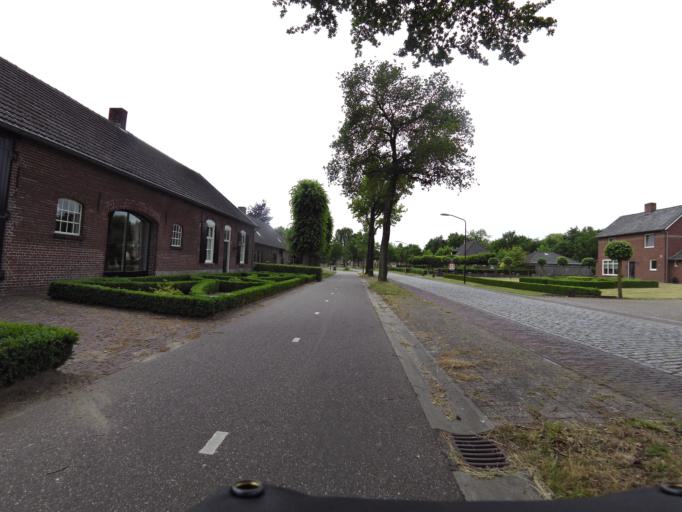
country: NL
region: North Brabant
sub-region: Gemeente Bladel en Netersel
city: Bladel
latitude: 51.3769
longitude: 5.2126
